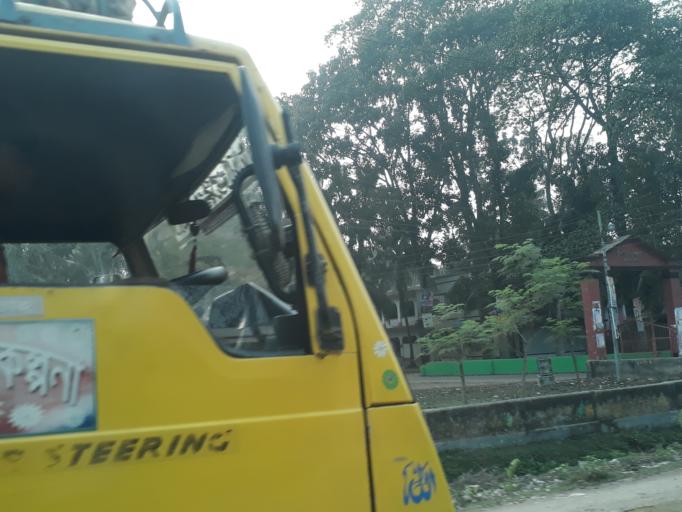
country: BD
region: Khulna
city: Bhatpara Abhaynagar
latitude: 22.9676
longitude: 89.4773
